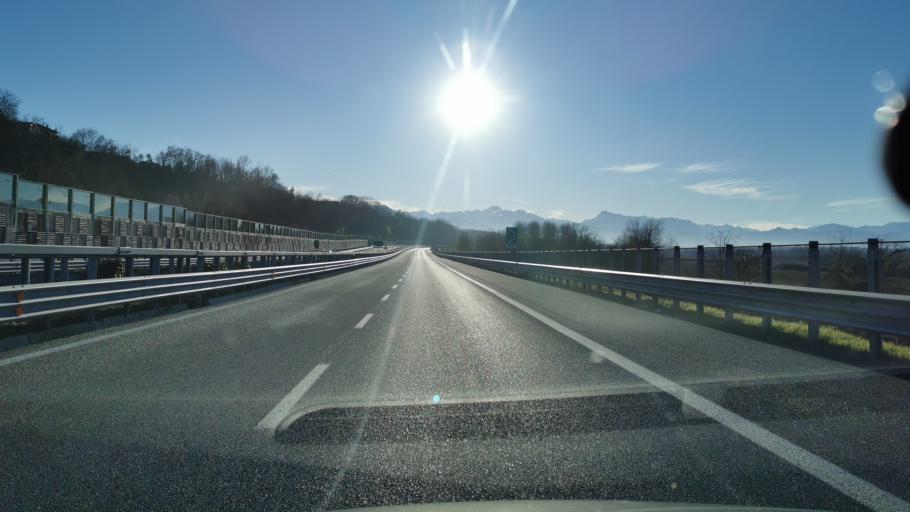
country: IT
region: Piedmont
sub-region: Provincia di Cuneo
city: Montanera
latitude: 44.4657
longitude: 7.6653
